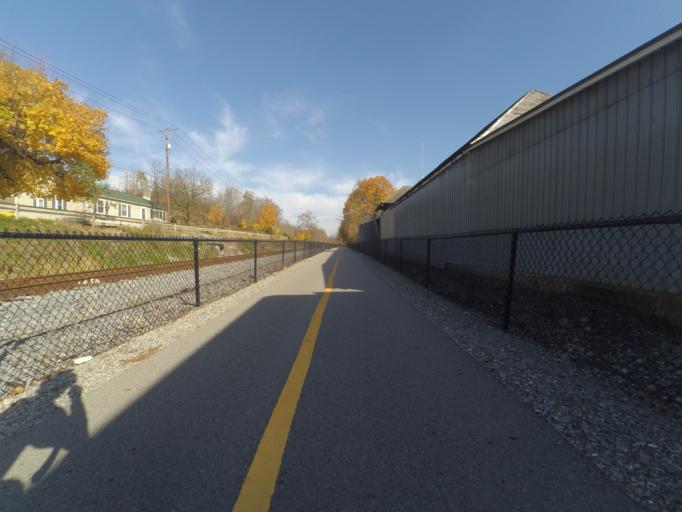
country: US
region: Pennsylvania
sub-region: Lycoming County
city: Jersey Shore
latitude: 41.2038
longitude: -77.2711
